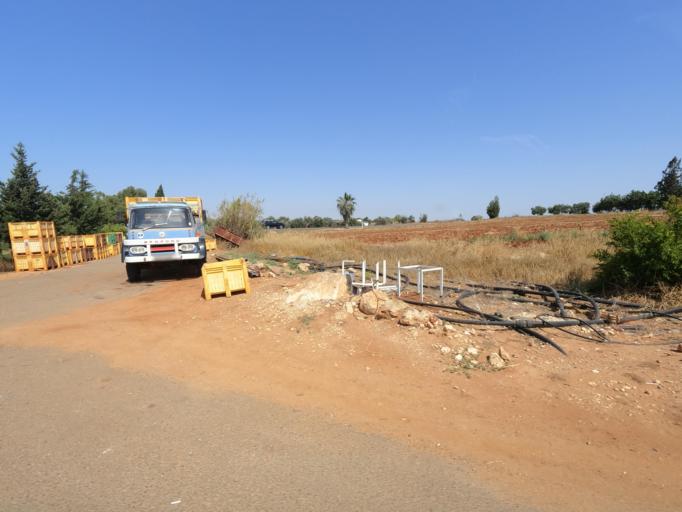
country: CY
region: Ammochostos
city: Liopetri
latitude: 34.9930
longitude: 33.9325
